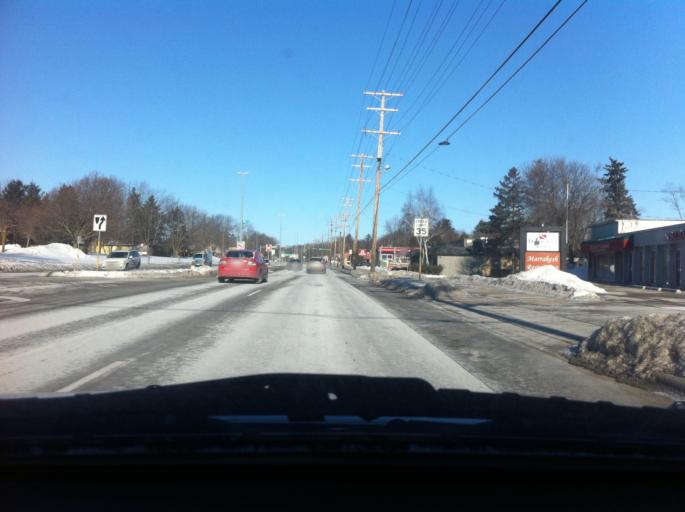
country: US
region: Wisconsin
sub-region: Dane County
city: Shorewood Hills
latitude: 43.0825
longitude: -89.4753
